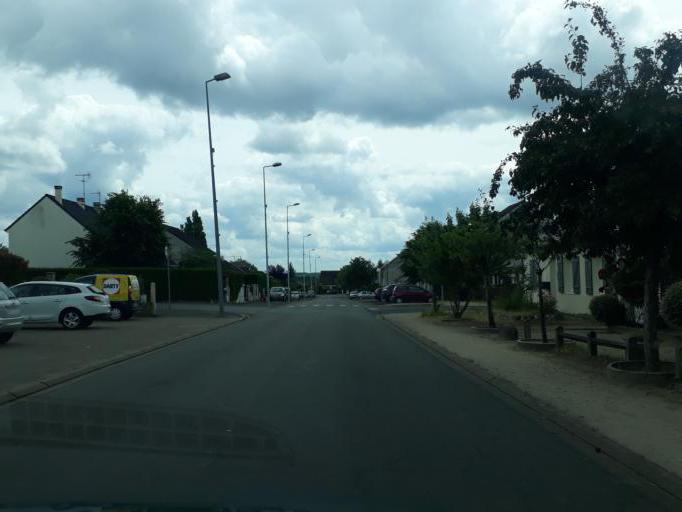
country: FR
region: Centre
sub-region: Departement du Loiret
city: Meung-sur-Loire
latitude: 47.8378
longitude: 1.7108
